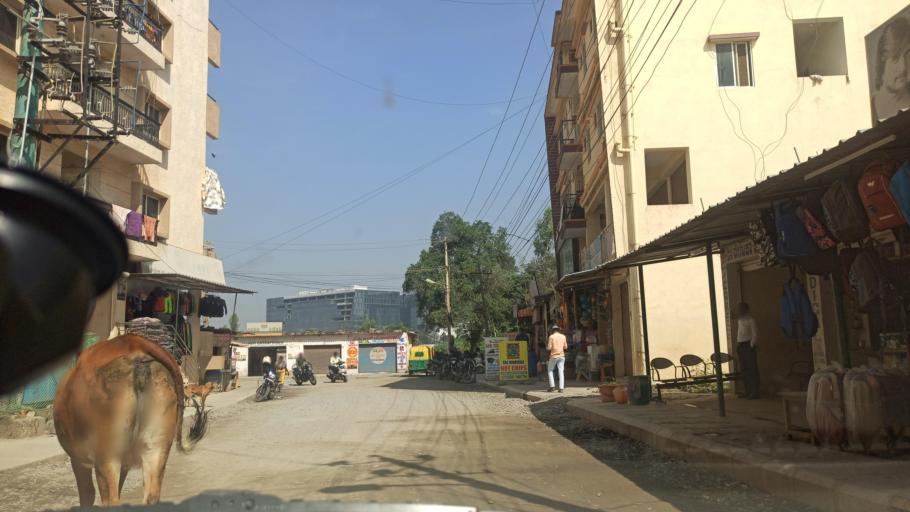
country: IN
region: Karnataka
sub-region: Bangalore Urban
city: Bangalore
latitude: 12.9274
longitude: 77.6894
